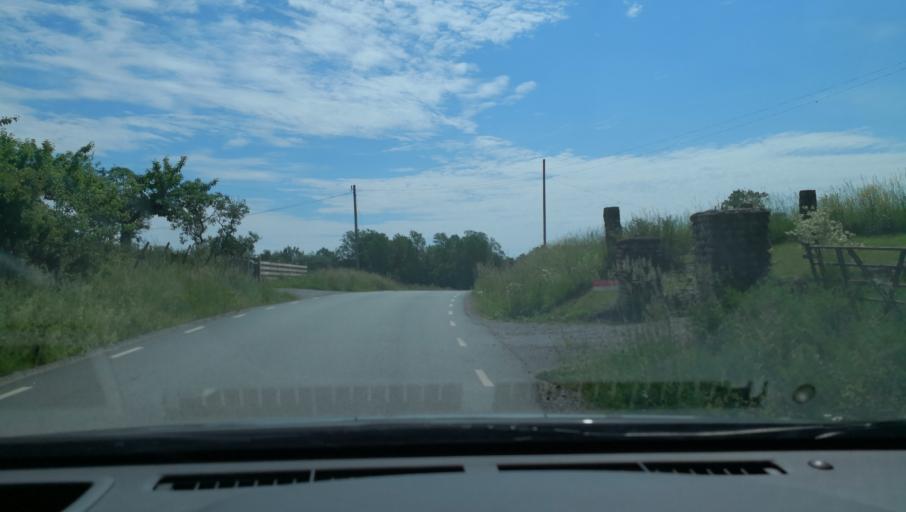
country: SE
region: Uppsala
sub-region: Habo Kommun
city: Balsta
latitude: 59.6803
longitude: 17.4665
